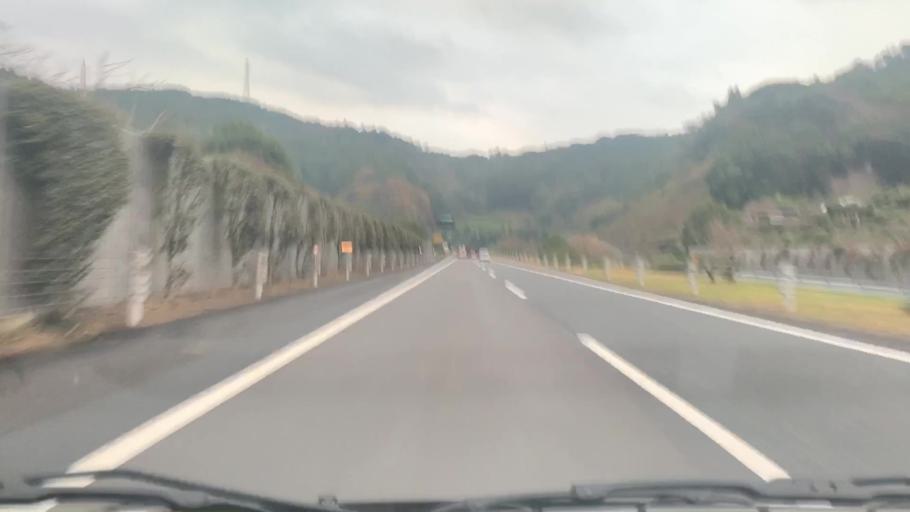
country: JP
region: Nagasaki
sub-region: Isahaya-shi
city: Isahaya
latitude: 32.8770
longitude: 129.9972
